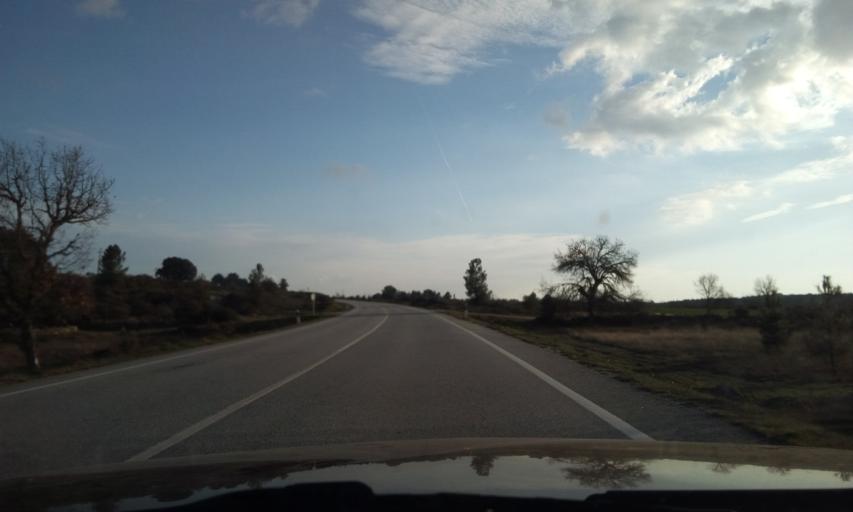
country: PT
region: Guarda
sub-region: Pinhel
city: Pinhel
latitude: 40.6363
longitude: -6.9728
